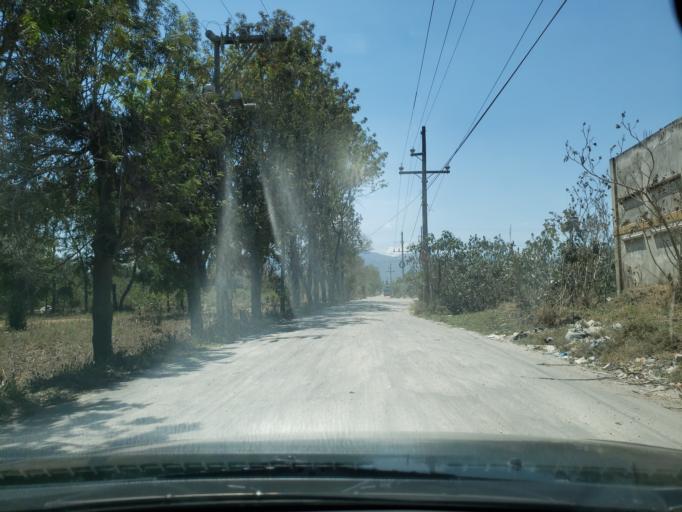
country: GT
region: Chimaltenango
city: El Tejar
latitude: 14.6492
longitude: -90.8023
